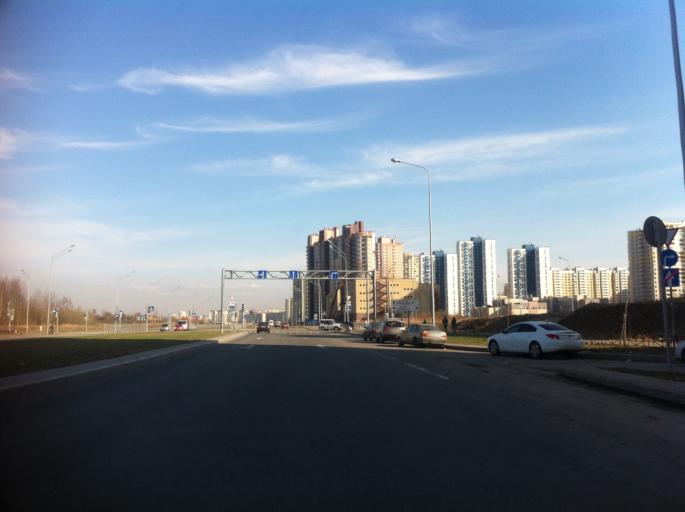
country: RU
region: St.-Petersburg
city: Uritsk
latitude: 59.8657
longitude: 30.1810
